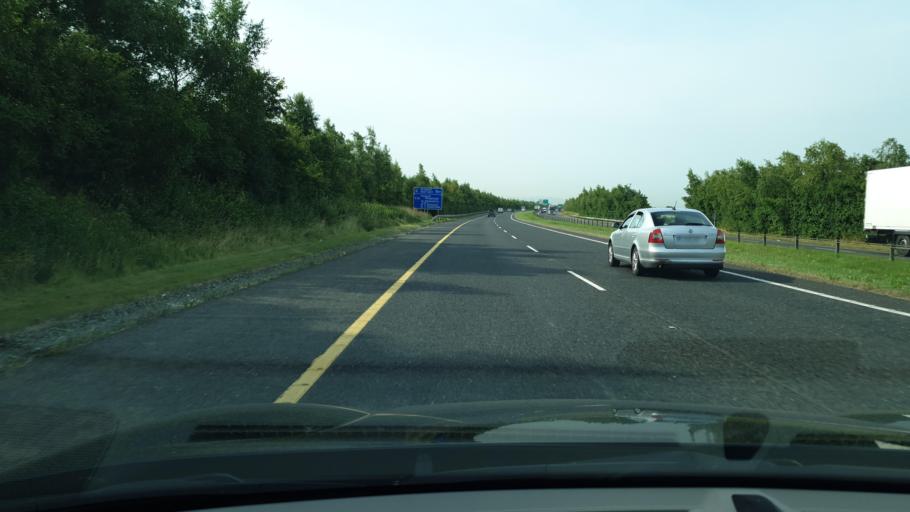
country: IE
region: Leinster
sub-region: Fingal County
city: Blanchardstown
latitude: 53.4556
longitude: -6.3545
